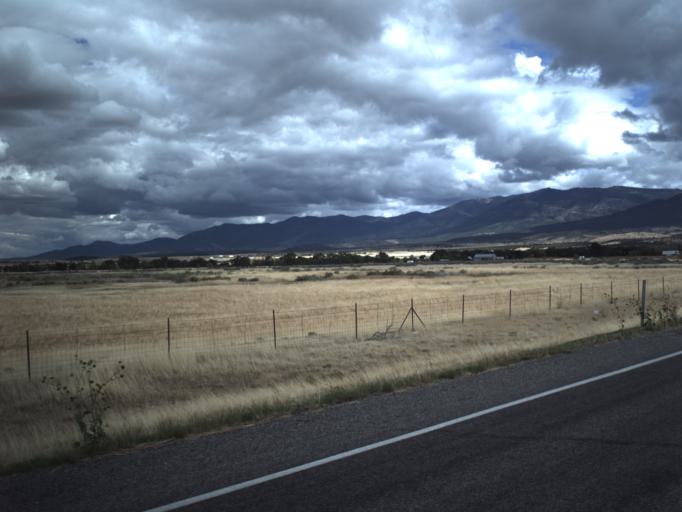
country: US
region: Utah
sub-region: Millard County
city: Fillmore
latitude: 38.9792
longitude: -112.3450
